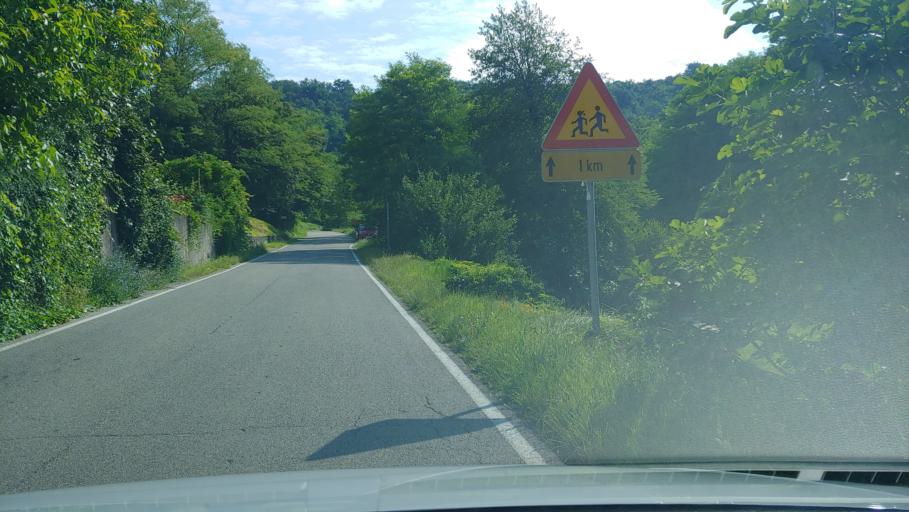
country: SI
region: Komen
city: Komen
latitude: 45.8628
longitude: 13.7857
